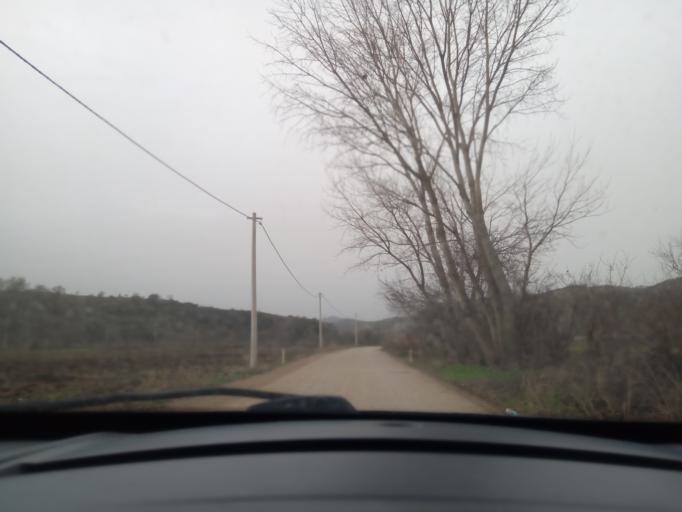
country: TR
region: Balikesir
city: Susurluk
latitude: 39.9200
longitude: 28.1366
